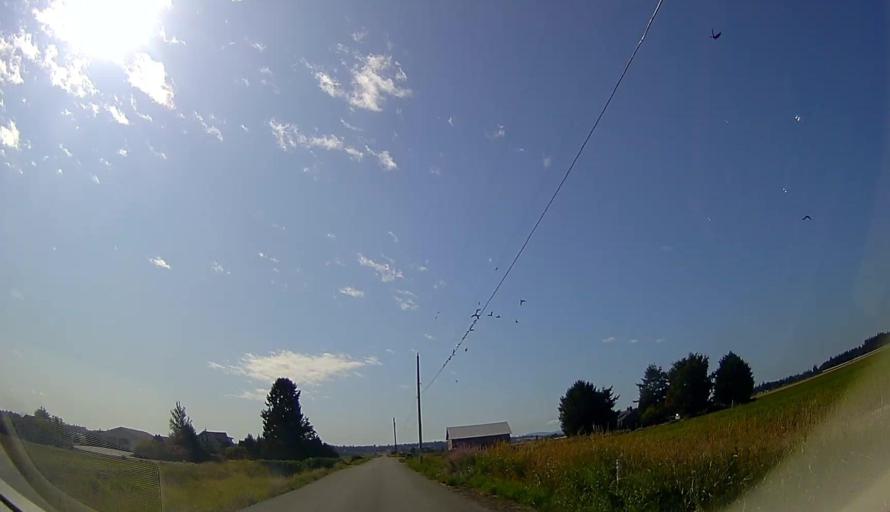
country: US
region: Washington
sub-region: Skagit County
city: Burlington
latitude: 48.4937
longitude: -122.3647
